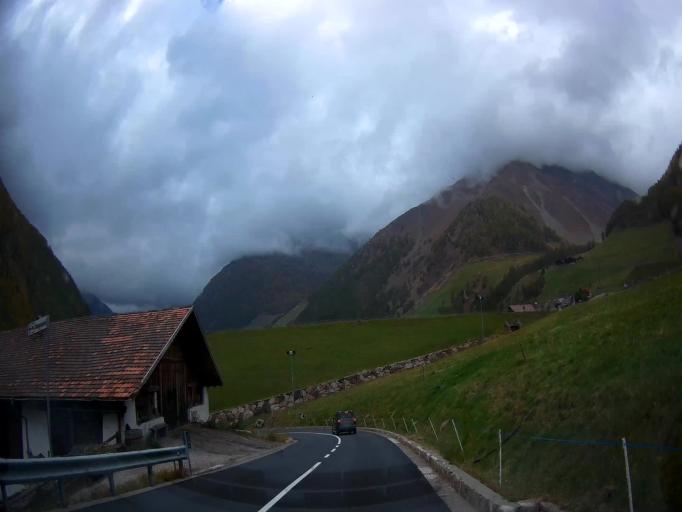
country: IT
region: Trentino-Alto Adige
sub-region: Bolzano
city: Senales
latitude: 46.7336
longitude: 10.8513
